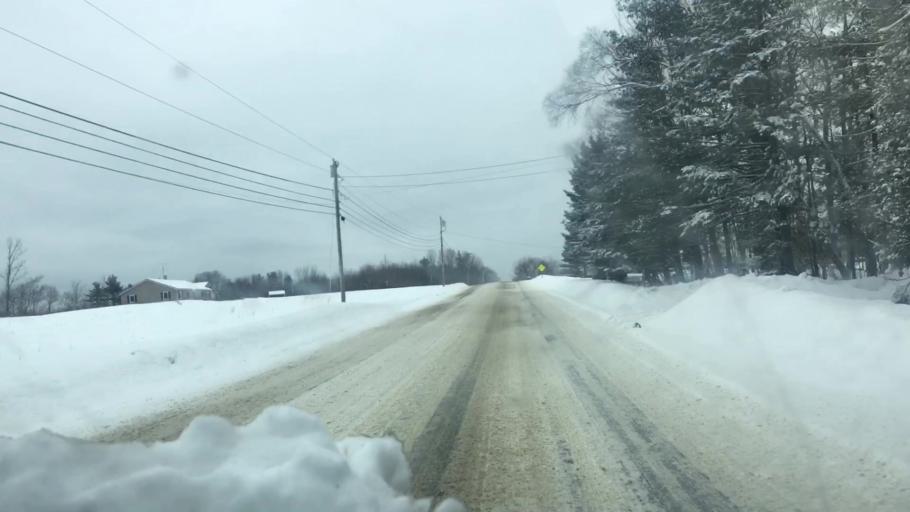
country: US
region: Maine
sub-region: Penobscot County
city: Bradford
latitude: 45.0124
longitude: -68.9891
